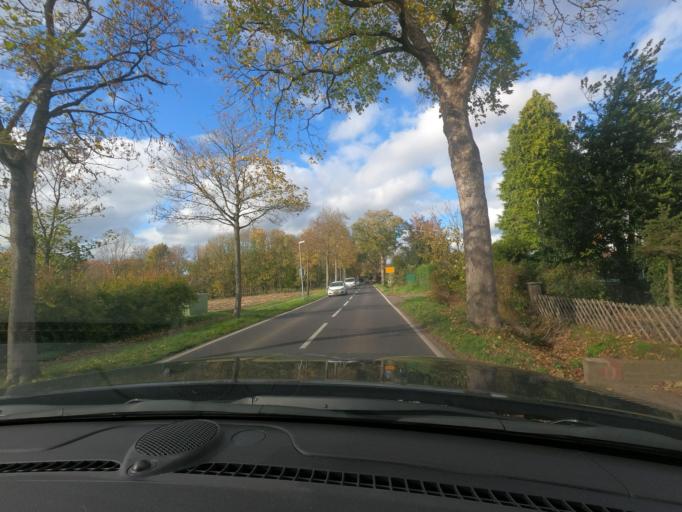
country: DE
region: North Rhine-Westphalia
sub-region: Regierungsbezirk Dusseldorf
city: Nettetal
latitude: 51.2670
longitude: 6.2735
